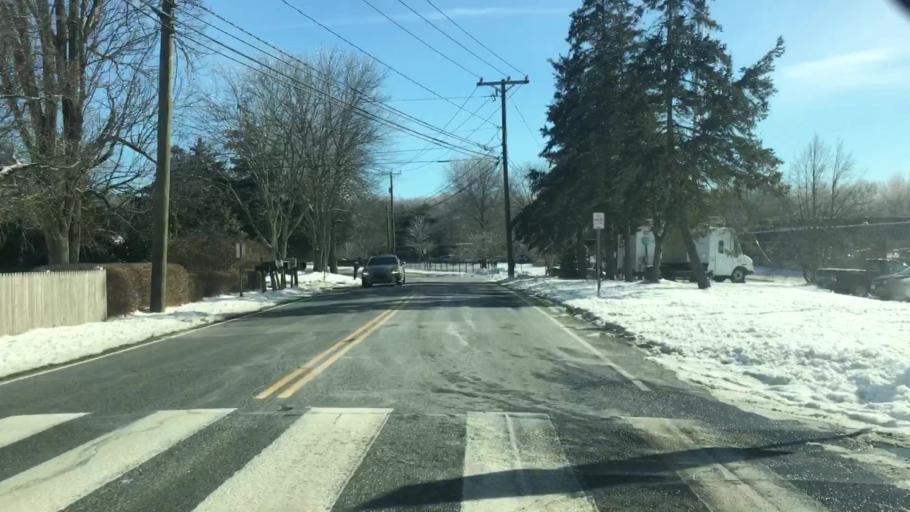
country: US
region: Connecticut
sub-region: Fairfield County
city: Newtown
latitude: 41.3467
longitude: -73.2311
